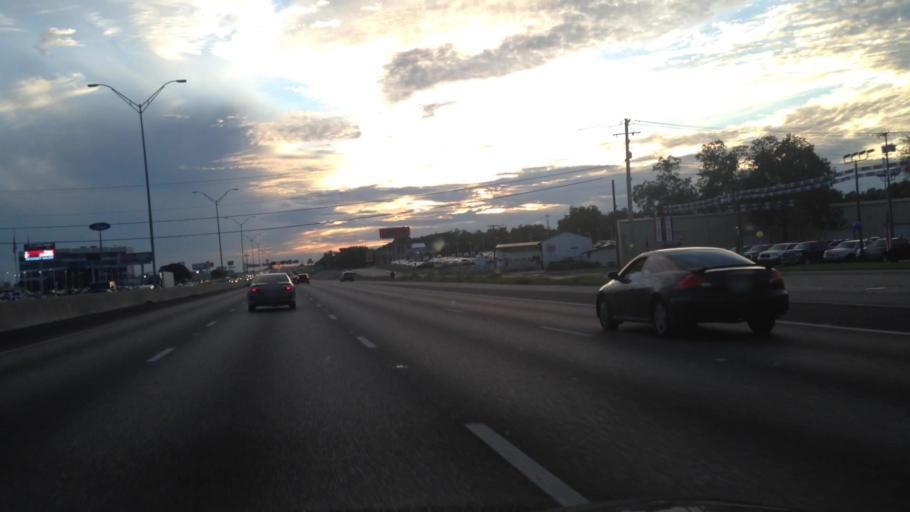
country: US
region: Texas
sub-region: Comal County
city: New Braunfels
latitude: 29.6901
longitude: -98.1133
